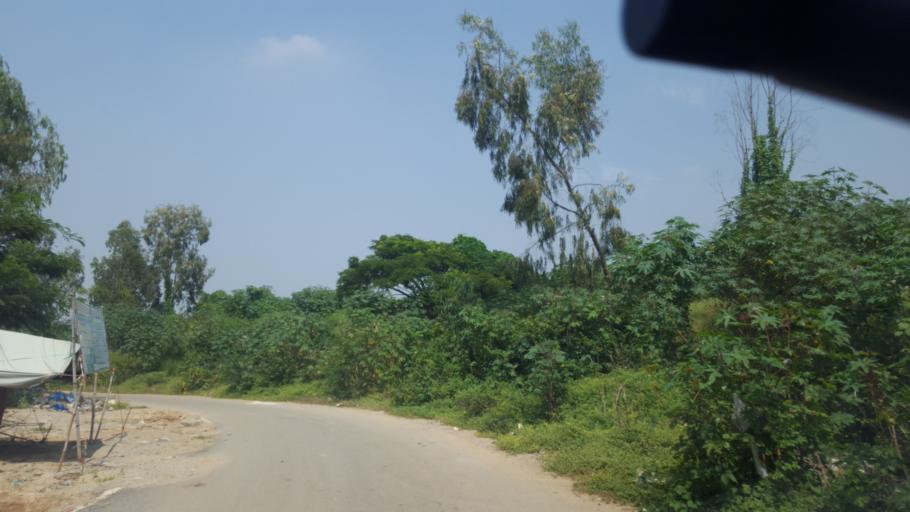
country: IN
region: Karnataka
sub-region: Bangalore Urban
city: Bangalore
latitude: 12.9385
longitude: 77.7079
